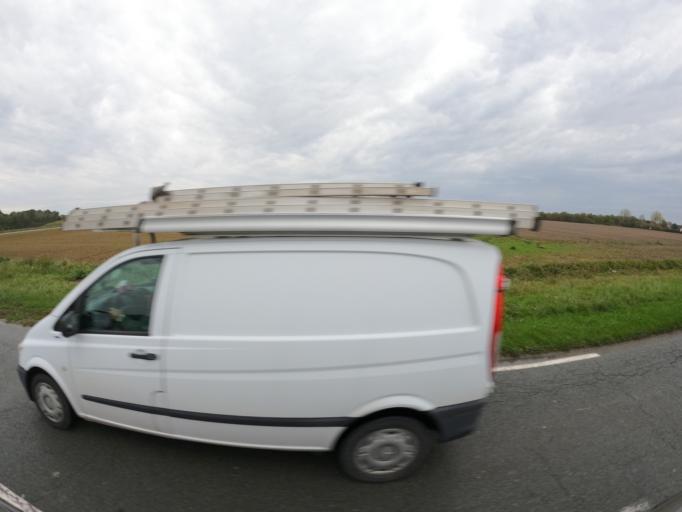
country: FR
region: Ile-de-France
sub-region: Departement de Seine-et-Marne
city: Villeneuve-le-Comte
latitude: 48.8176
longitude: 2.8199
